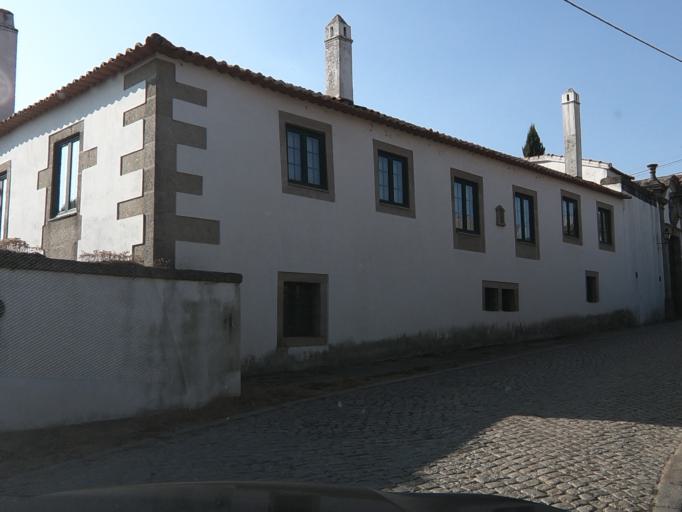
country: PT
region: Vila Real
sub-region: Sabrosa
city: Vilela
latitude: 41.2262
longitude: -7.6362
